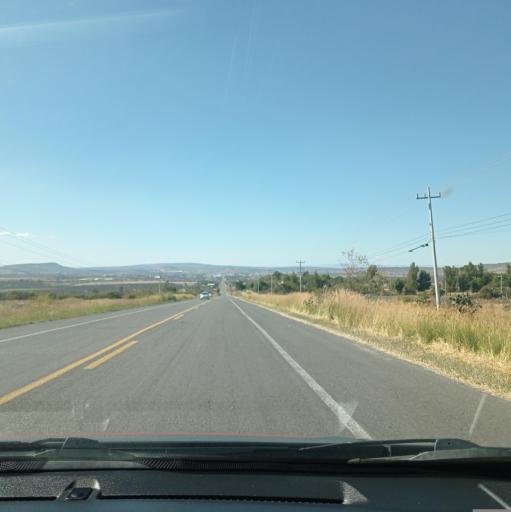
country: MX
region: Jalisco
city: San Miguel el Alto
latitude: 21.0157
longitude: -102.3277
